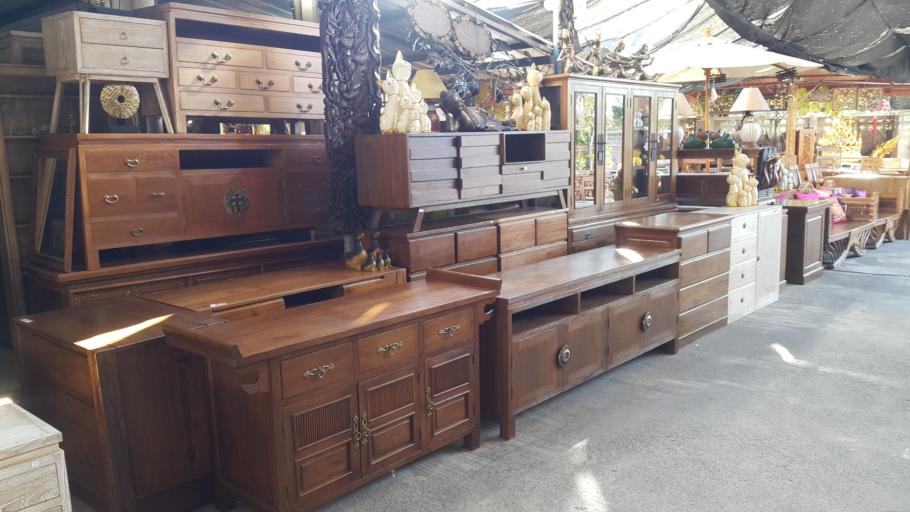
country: TH
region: Chiang Mai
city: Hang Dong
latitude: 18.6875
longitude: 98.9454
